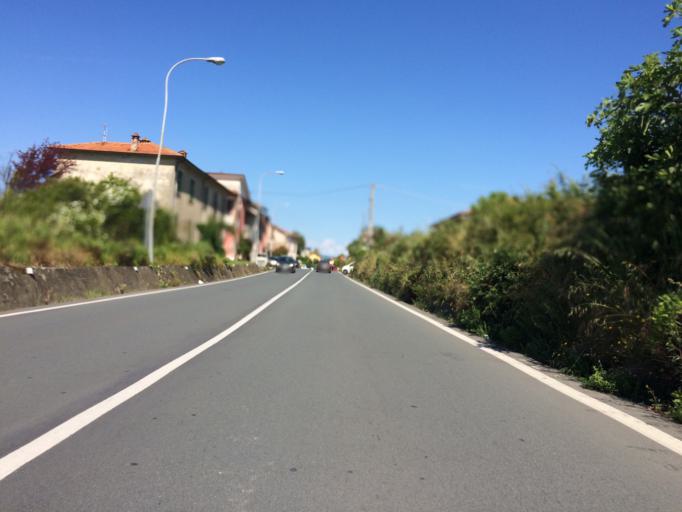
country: IT
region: Liguria
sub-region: Provincia di La Spezia
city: Colombiera-Molicciara
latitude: 44.0898
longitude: 9.9995
